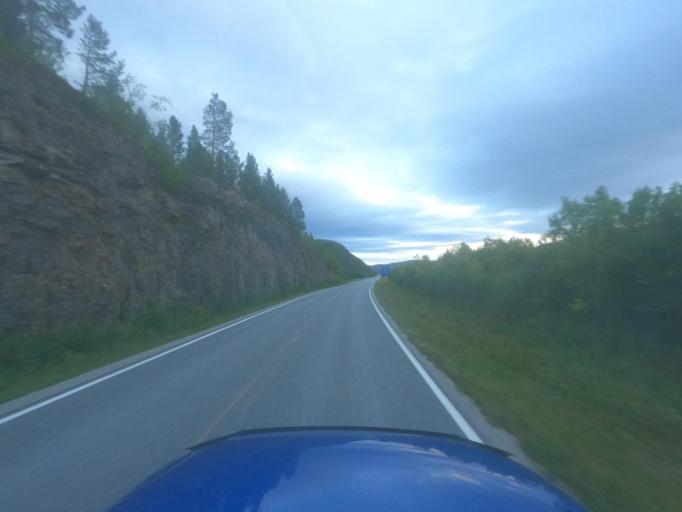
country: NO
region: Finnmark Fylke
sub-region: Porsanger
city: Lakselv
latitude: 69.9273
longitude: 24.9828
